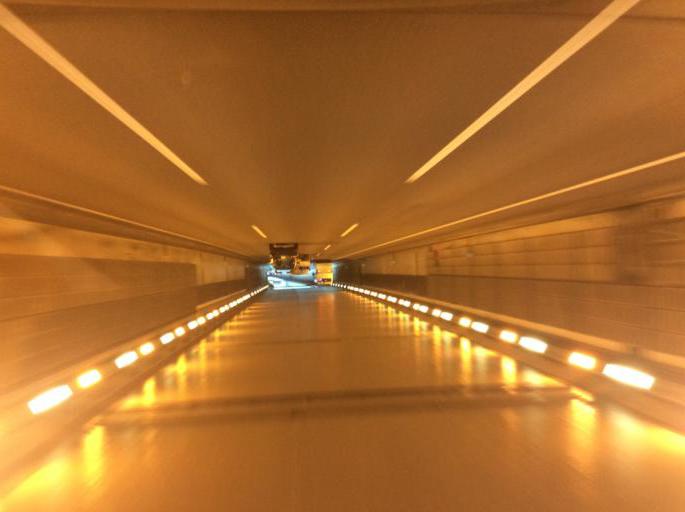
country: JP
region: Chiba
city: Nagareyama
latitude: 35.9028
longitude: 139.9287
